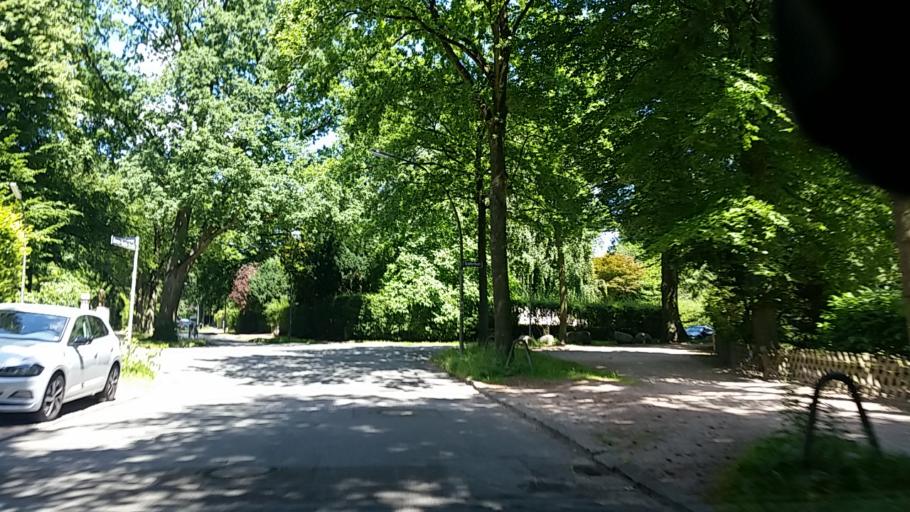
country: DE
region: Hamburg
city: Eidelstedt
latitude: 53.5624
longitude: 9.8690
